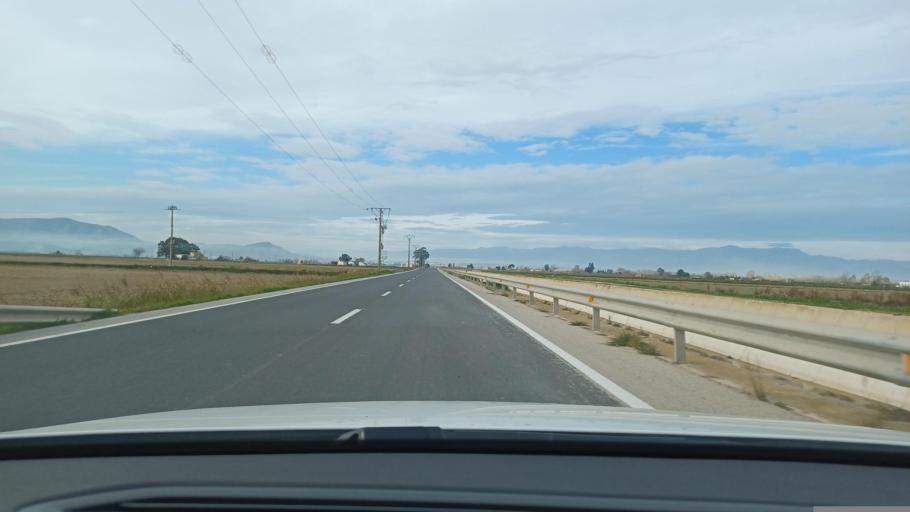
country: ES
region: Catalonia
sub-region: Provincia de Tarragona
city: Deltebre
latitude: 40.7109
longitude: 0.6703
